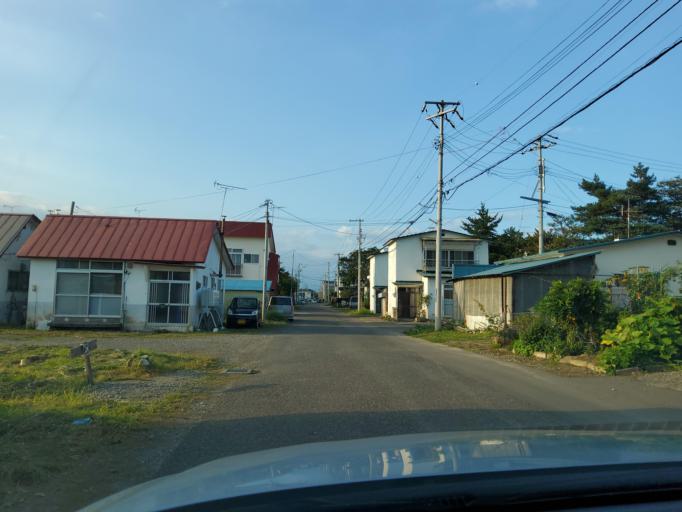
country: JP
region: Hokkaido
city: Obihiro
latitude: 42.9320
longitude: 143.1892
